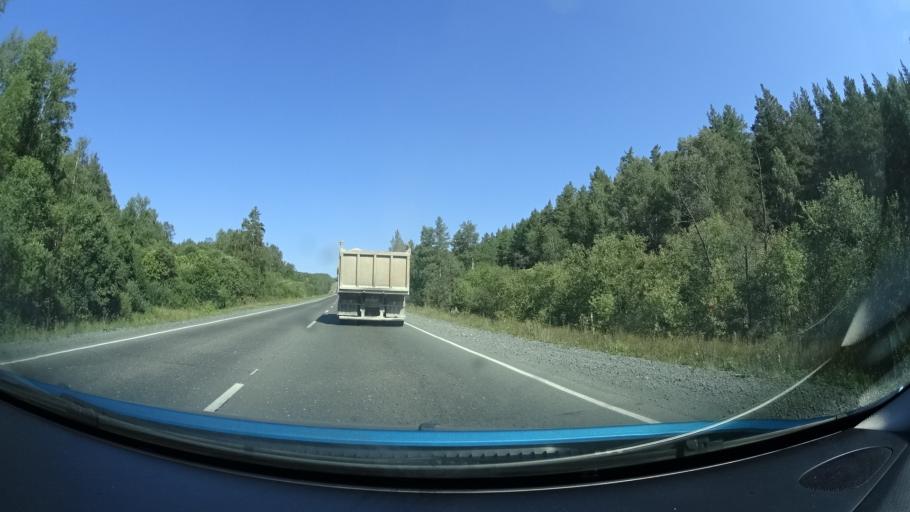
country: RU
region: Bashkortostan
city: Abzakovo
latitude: 53.8709
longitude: 58.5373
